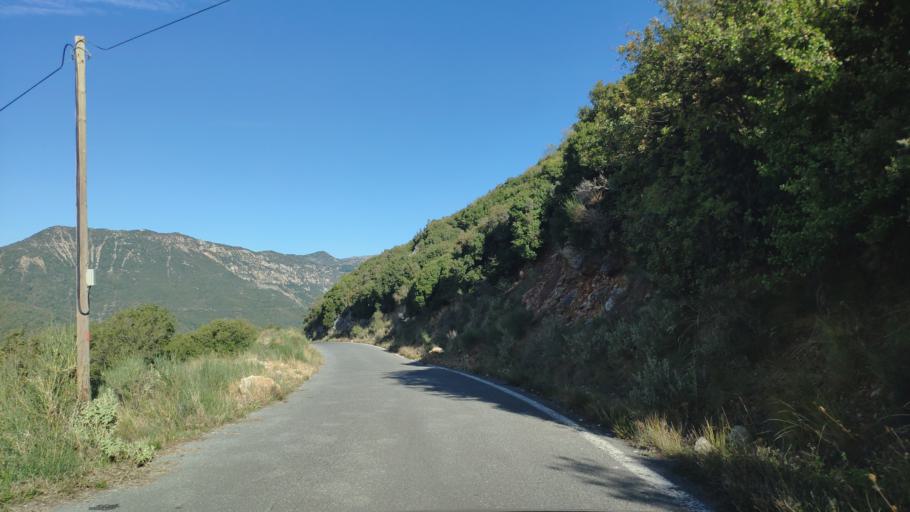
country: GR
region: Peloponnese
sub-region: Nomos Arkadias
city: Dimitsana
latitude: 37.5508
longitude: 22.0620
